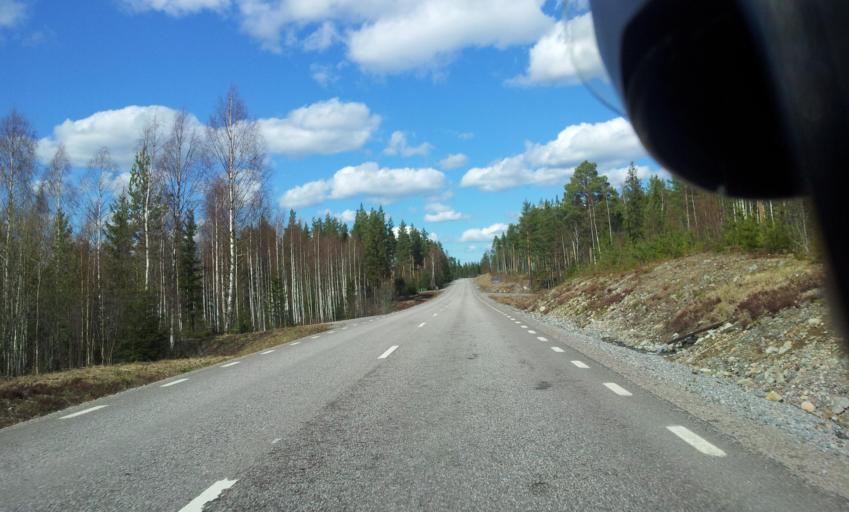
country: SE
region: Gaevleborg
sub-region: Ovanakers Kommun
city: Edsbyn
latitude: 61.2194
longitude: 15.8772
